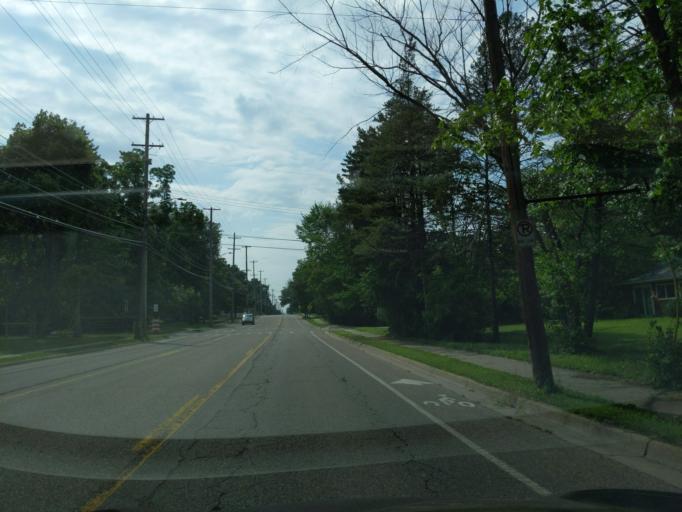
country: US
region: Michigan
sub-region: Ingham County
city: East Lansing
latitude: 42.7407
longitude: -84.4677
